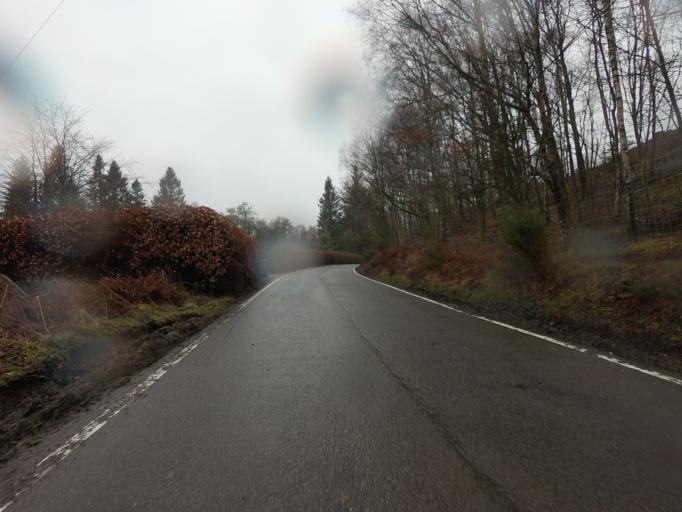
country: GB
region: Scotland
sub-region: Stirling
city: Killearn
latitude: 56.1892
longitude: -4.4960
